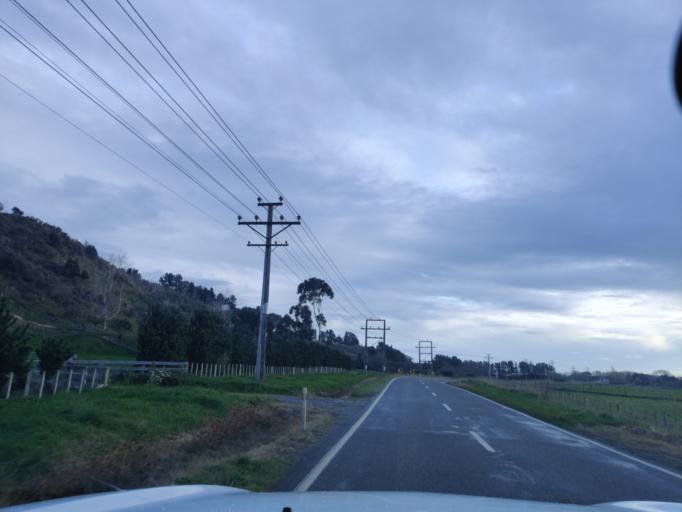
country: NZ
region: Manawatu-Wanganui
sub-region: Palmerston North City
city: Palmerston North
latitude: -40.3589
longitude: 175.6818
